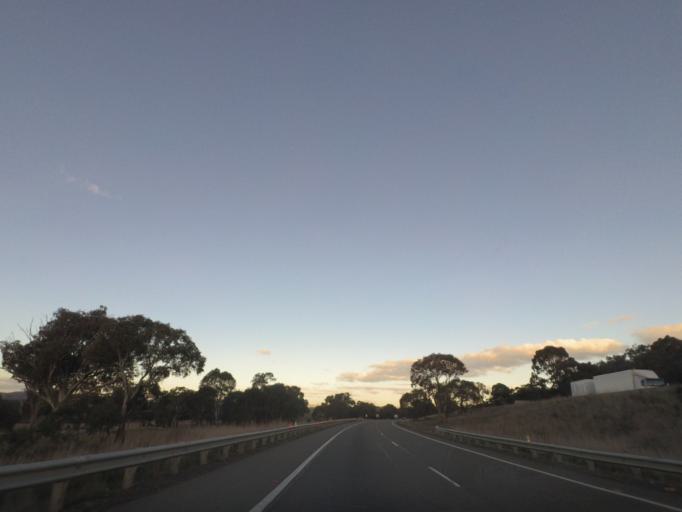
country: AU
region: New South Wales
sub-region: Yass Valley
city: Yass
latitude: -34.7725
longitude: 148.8349
